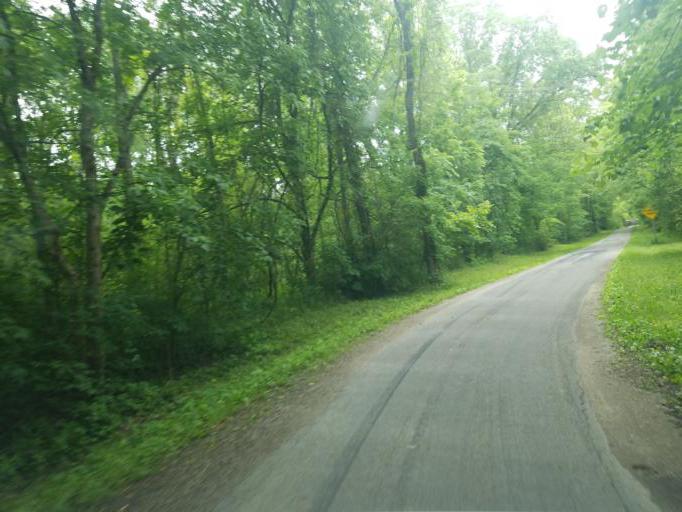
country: US
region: Ohio
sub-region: Morrow County
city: Cardington
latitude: 40.5307
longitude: -83.0143
